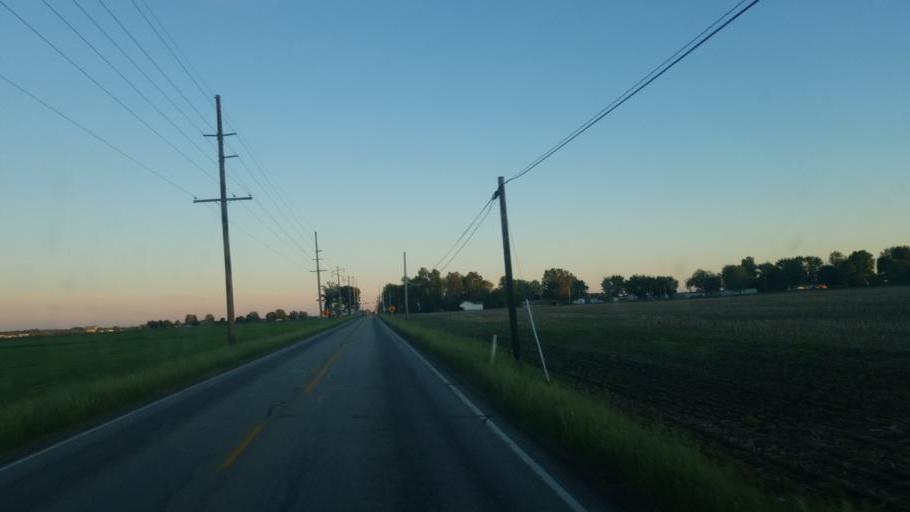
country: US
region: Indiana
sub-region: Elkhart County
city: Nappanee
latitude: 41.3645
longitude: -86.0006
